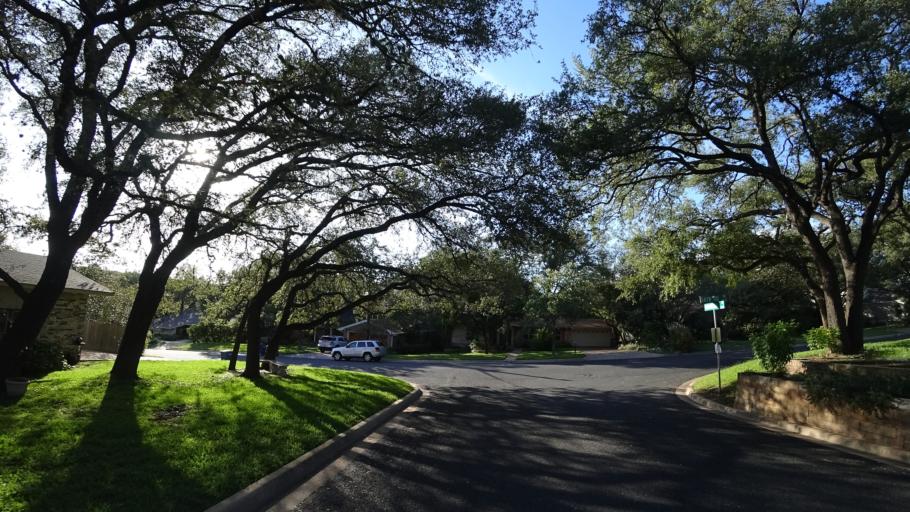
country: US
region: Texas
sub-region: Williamson County
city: Jollyville
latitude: 30.3666
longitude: -97.7486
